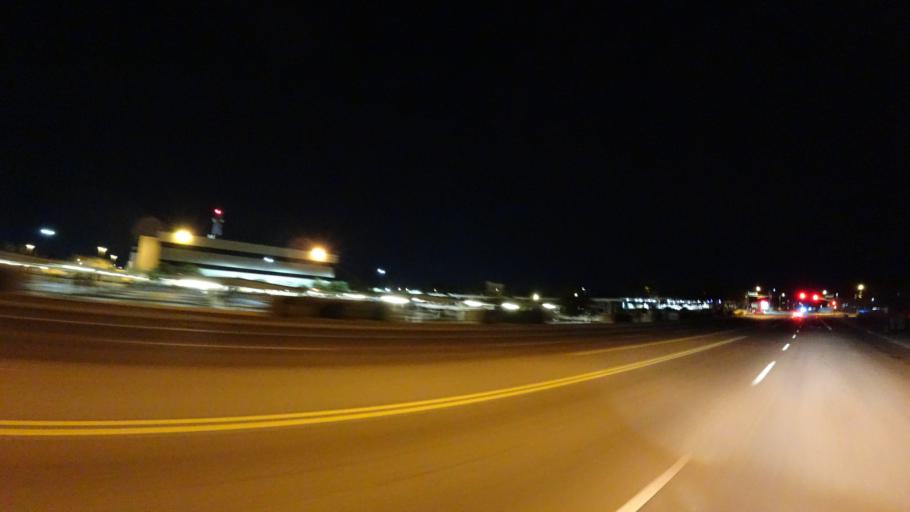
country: US
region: Arizona
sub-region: Maricopa County
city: Tempe Junction
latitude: 33.4641
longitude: -111.9697
